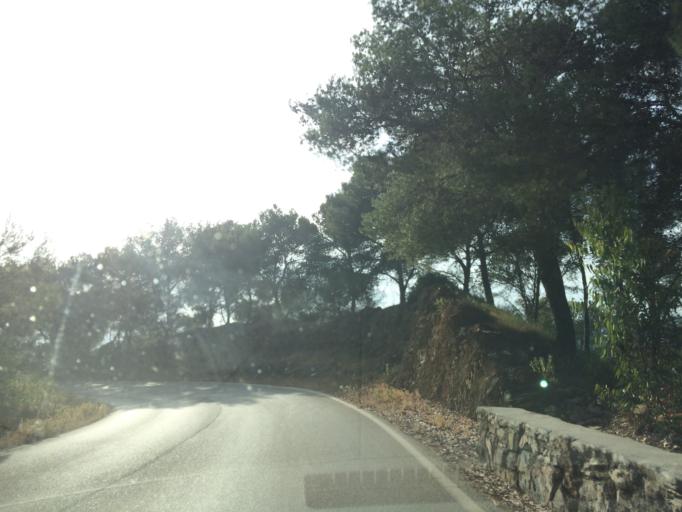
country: ES
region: Andalusia
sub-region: Provincia de Malaga
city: Malaga
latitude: 36.7690
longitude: -4.3933
